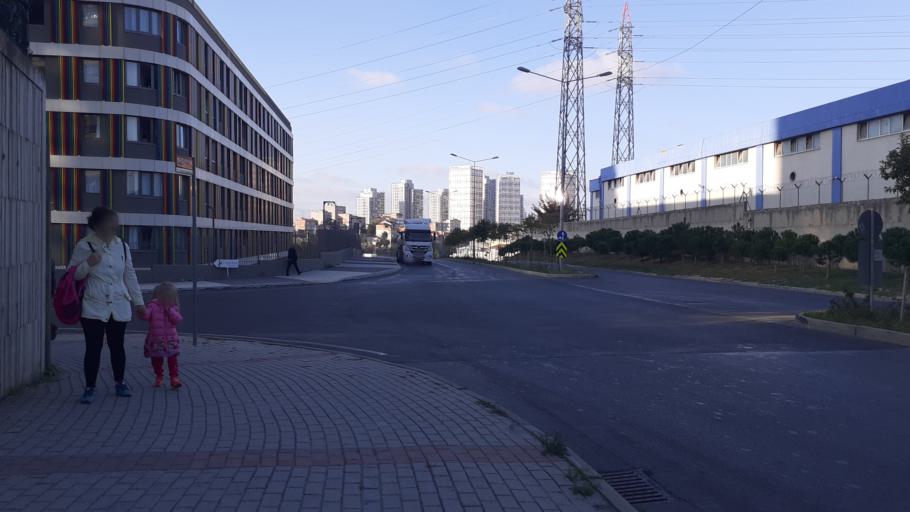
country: TR
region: Istanbul
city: Basaksehir
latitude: 41.0662
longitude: 28.7804
